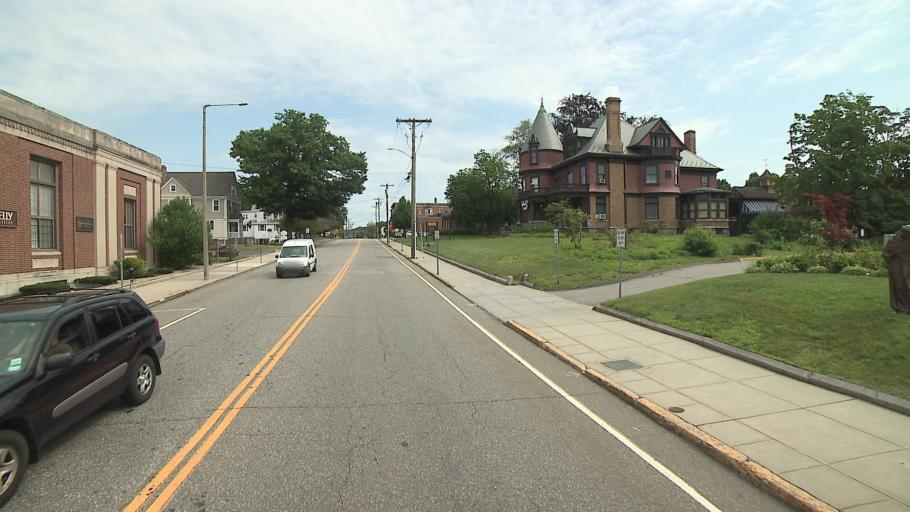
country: US
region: Connecticut
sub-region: Litchfield County
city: Torrington
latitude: 41.8039
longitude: -73.1214
